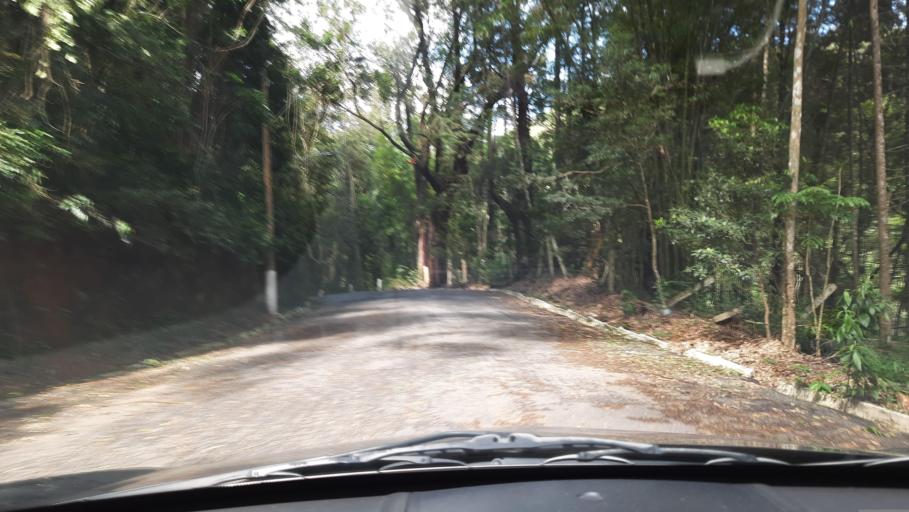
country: BR
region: Minas Gerais
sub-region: Pocos De Caldas
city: Pocos de Caldas
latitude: -21.7775
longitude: -46.5581
